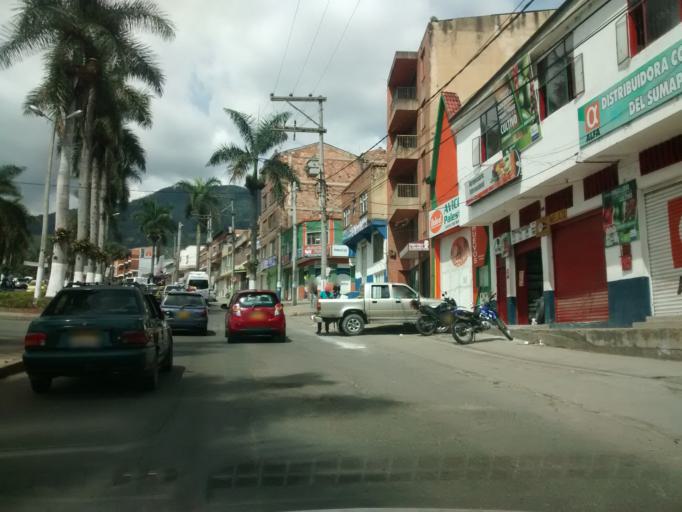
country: CO
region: Cundinamarca
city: Fusagasuga
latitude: 4.3411
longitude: -74.3663
